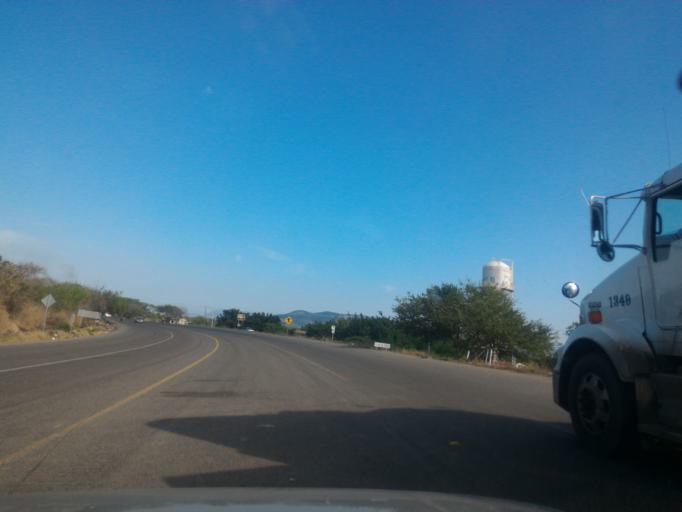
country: MX
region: Michoacan
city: Coahuayana Viejo
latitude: 18.7559
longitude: -103.7246
